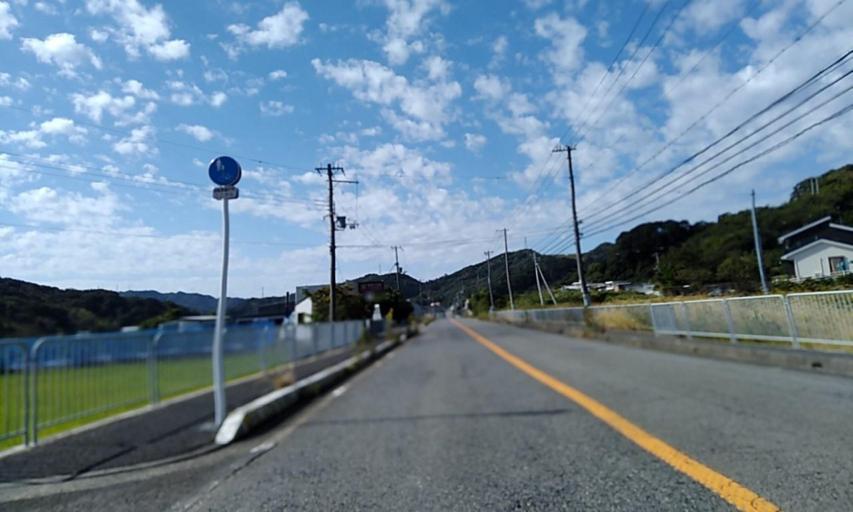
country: JP
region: Wakayama
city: Gobo
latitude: 33.9731
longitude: 135.1364
